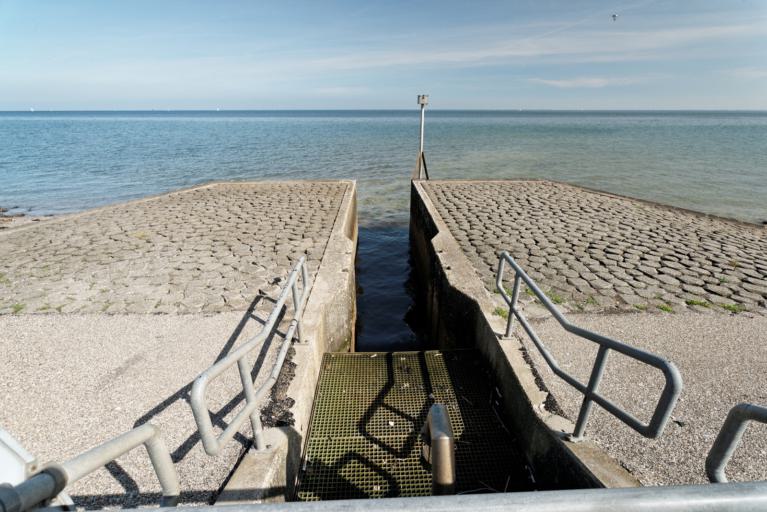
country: NL
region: North Holland
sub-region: Gemeente Texel
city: Den Burg
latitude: 53.0176
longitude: 4.8042
